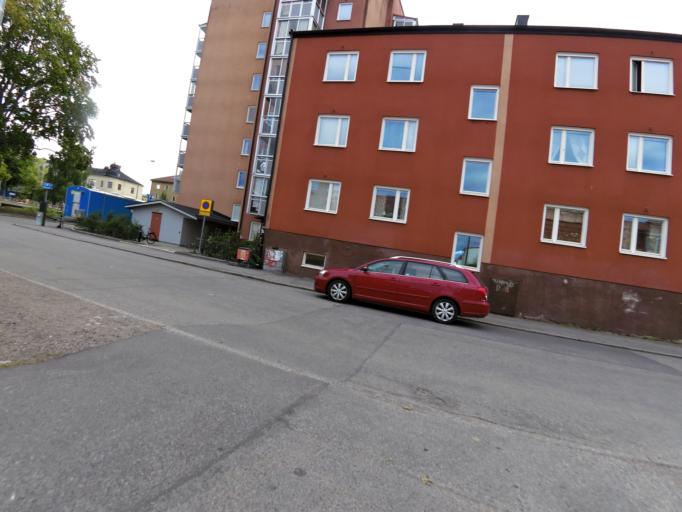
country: SE
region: Gaevleborg
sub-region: Gavle Kommun
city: Gavle
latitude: 60.6692
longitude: 17.1511
